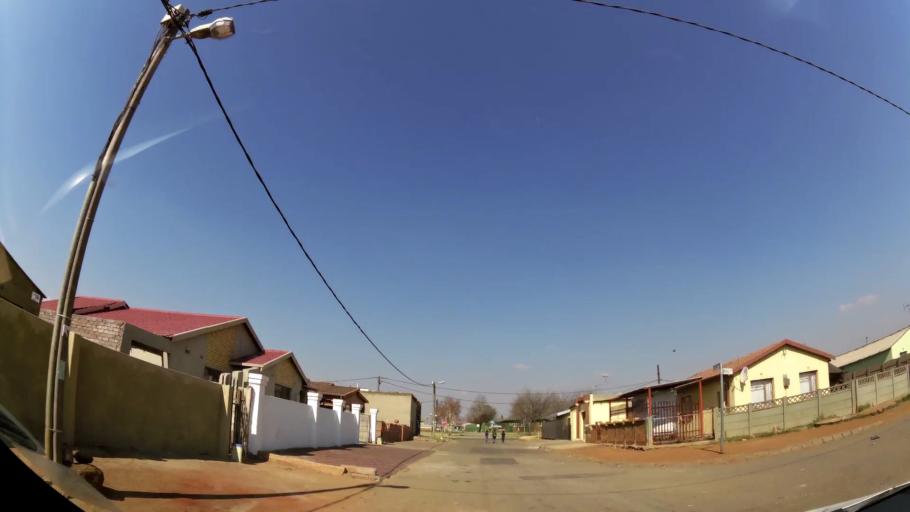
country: ZA
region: Gauteng
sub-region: Ekurhuleni Metropolitan Municipality
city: Boksburg
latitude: -26.2147
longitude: 28.2913
